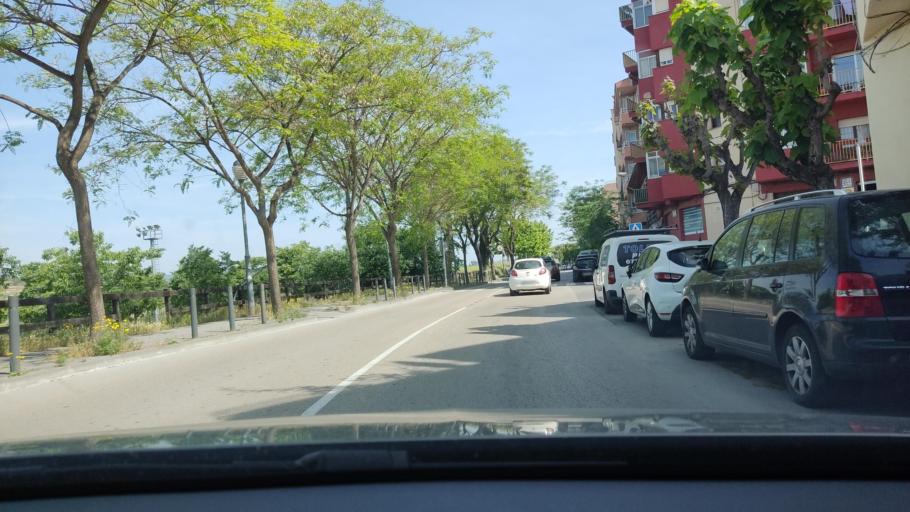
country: ES
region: Catalonia
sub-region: Provincia de Barcelona
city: Vilafranca del Penedes
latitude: 41.3539
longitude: 1.7008
